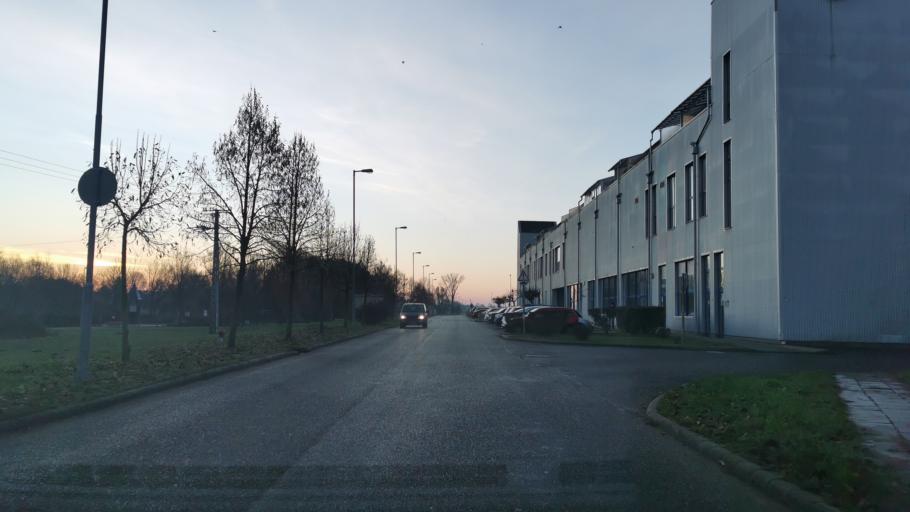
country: HU
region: Hajdu-Bihar
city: Debrecen
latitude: 47.5984
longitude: 21.5788
